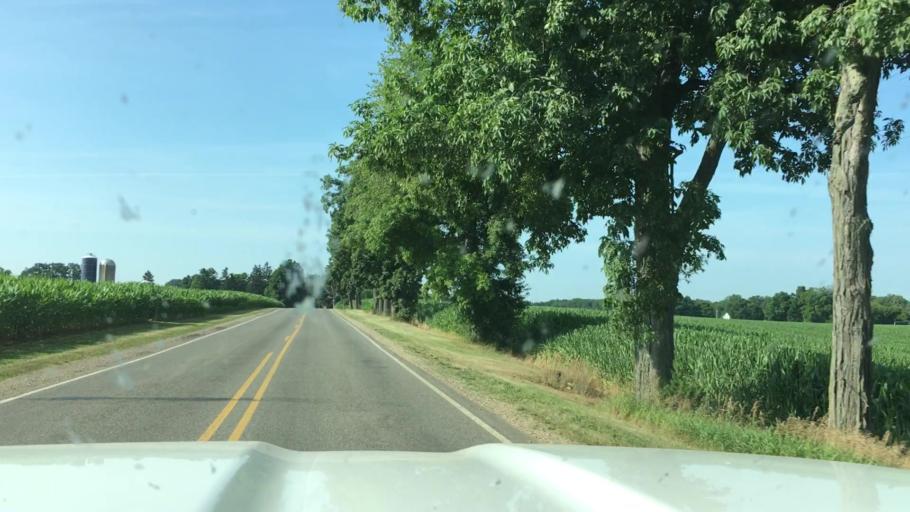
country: US
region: Michigan
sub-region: Barry County
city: Stony Point
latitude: 42.4613
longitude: -85.4447
